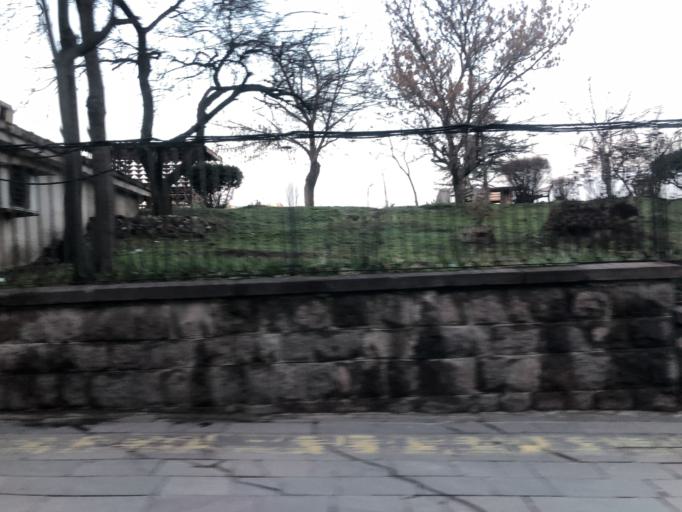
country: TR
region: Ankara
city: Ankara
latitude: 39.9466
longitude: 32.8550
